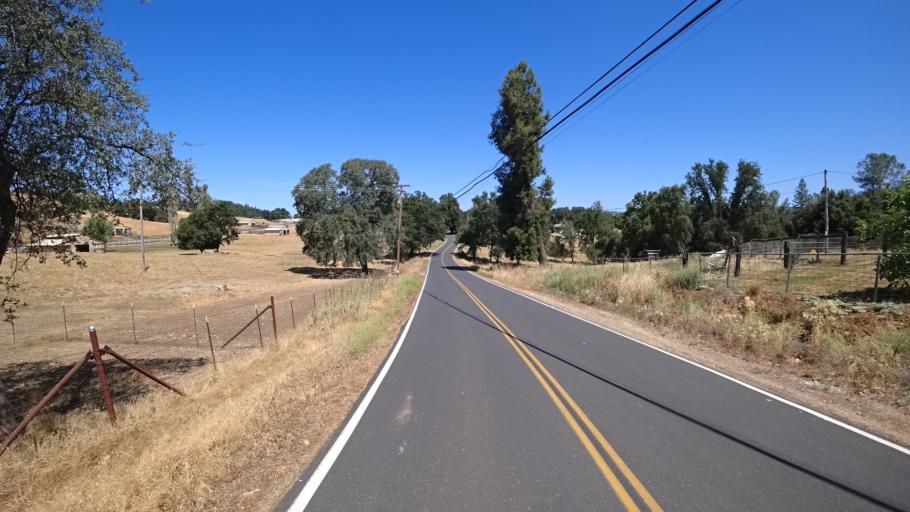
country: US
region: California
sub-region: Calaveras County
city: Mountain Ranch
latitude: 38.2177
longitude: -120.5426
